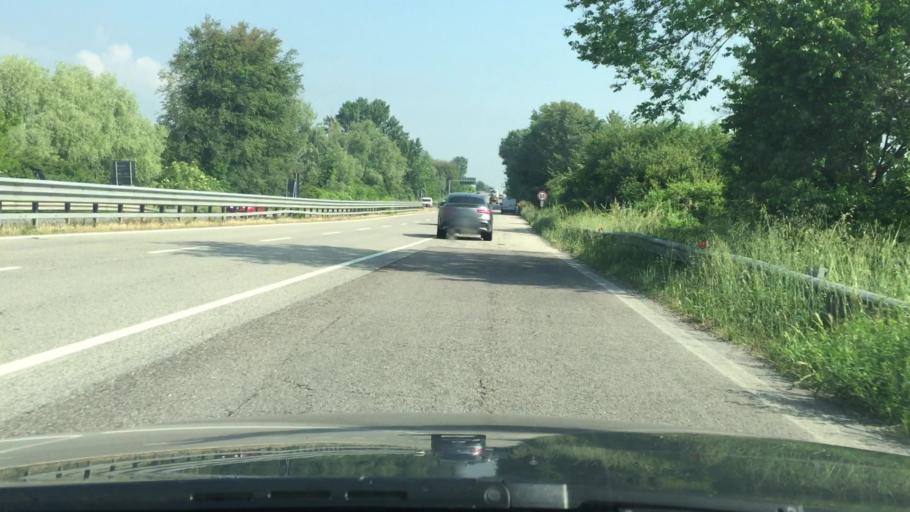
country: IT
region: Emilia-Romagna
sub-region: Provincia di Ferrara
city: Gaibanella-Sant'Edigio
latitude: 44.7969
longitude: 11.6371
